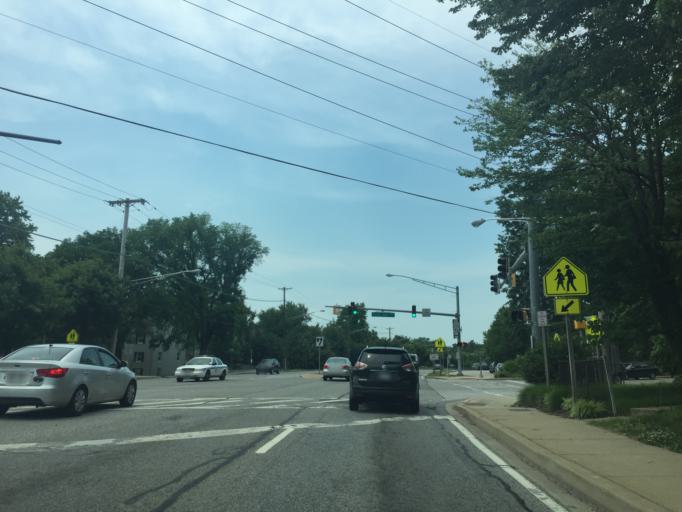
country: US
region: Maryland
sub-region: Baltimore County
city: Parkville
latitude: 39.3919
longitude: -76.5654
